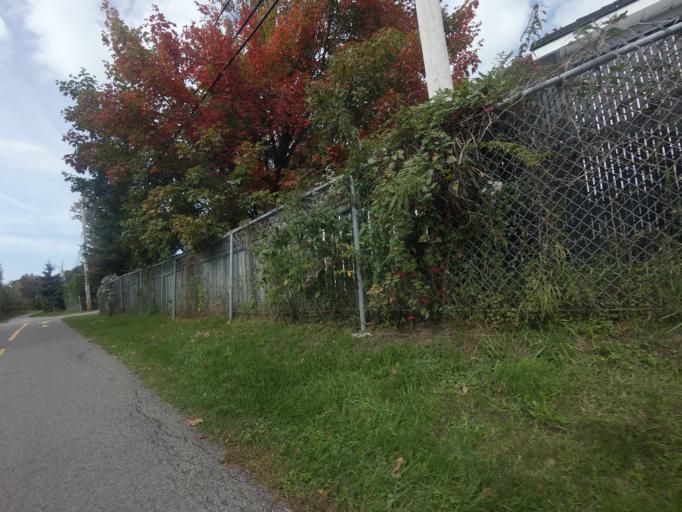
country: CA
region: Quebec
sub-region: Laurentides
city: Blainville
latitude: 45.6914
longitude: -73.8908
